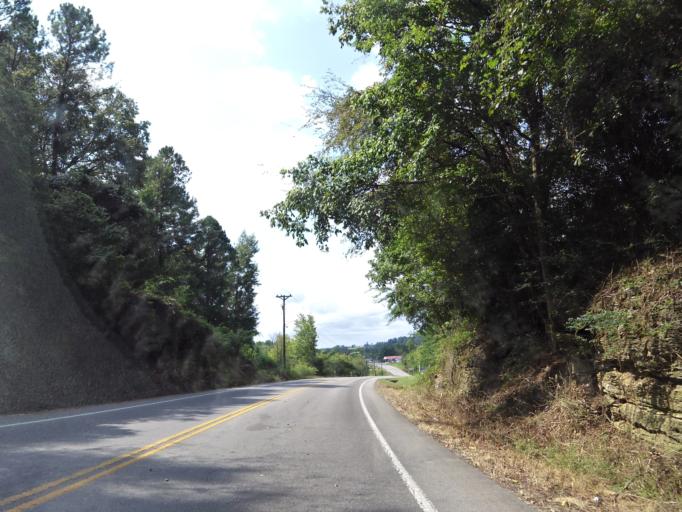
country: US
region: Tennessee
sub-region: Perry County
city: Linden
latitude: 35.7792
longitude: -87.7776
